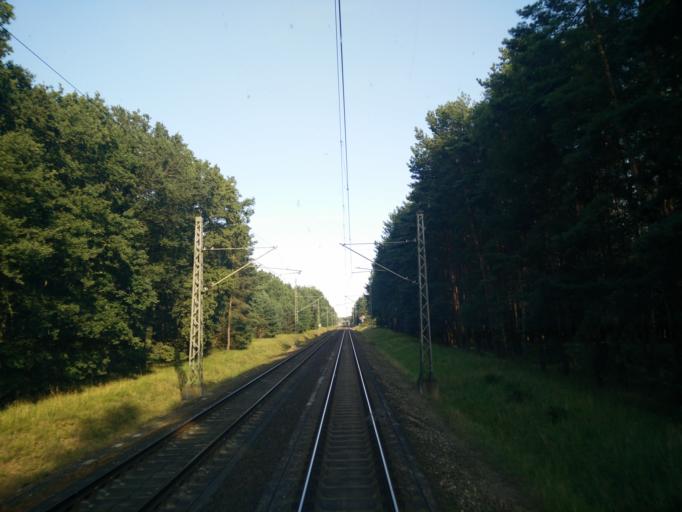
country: DE
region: Saxony-Anhalt
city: Havelberg
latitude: 52.8956
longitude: 12.1209
